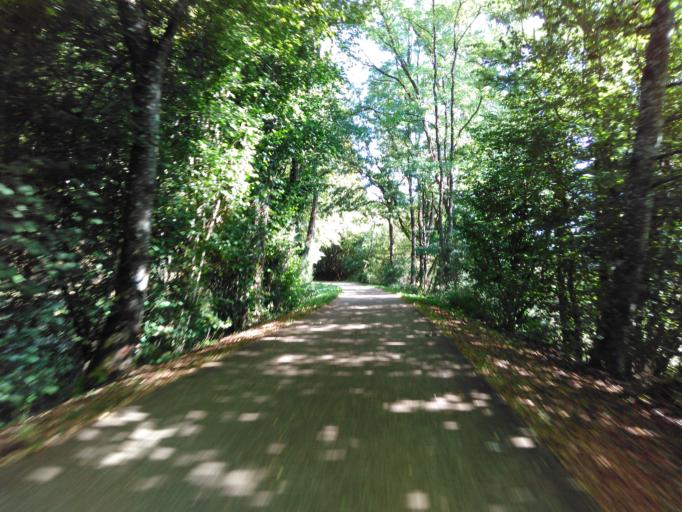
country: LU
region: Luxembourg
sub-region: Canton de Capellen
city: Hobscheid
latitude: 49.6928
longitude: 5.9016
